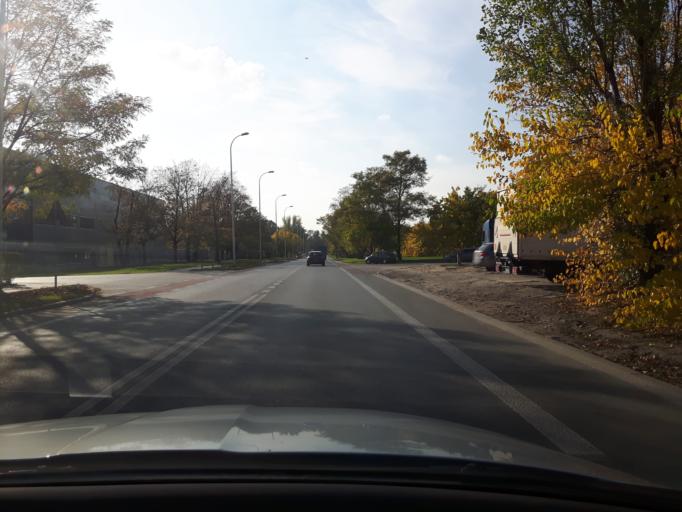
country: PL
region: Masovian Voivodeship
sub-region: Warszawa
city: Targowek
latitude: 52.3053
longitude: 21.0161
